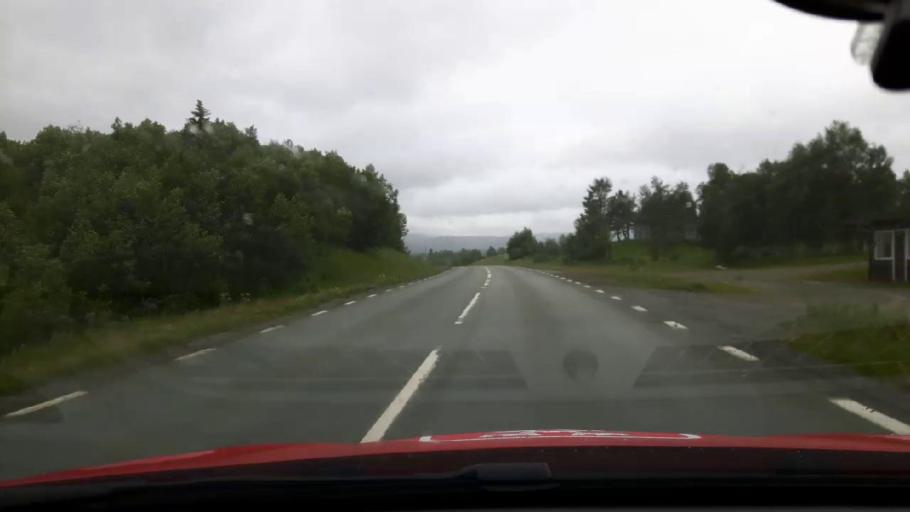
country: NO
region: Nord-Trondelag
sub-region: Meraker
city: Meraker
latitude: 63.2833
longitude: 12.1278
